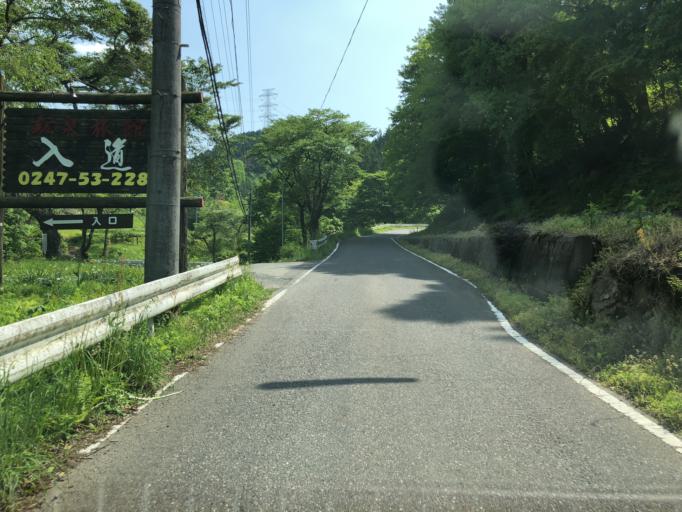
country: JP
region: Fukushima
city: Ishikawa
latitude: 37.0283
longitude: 140.5646
